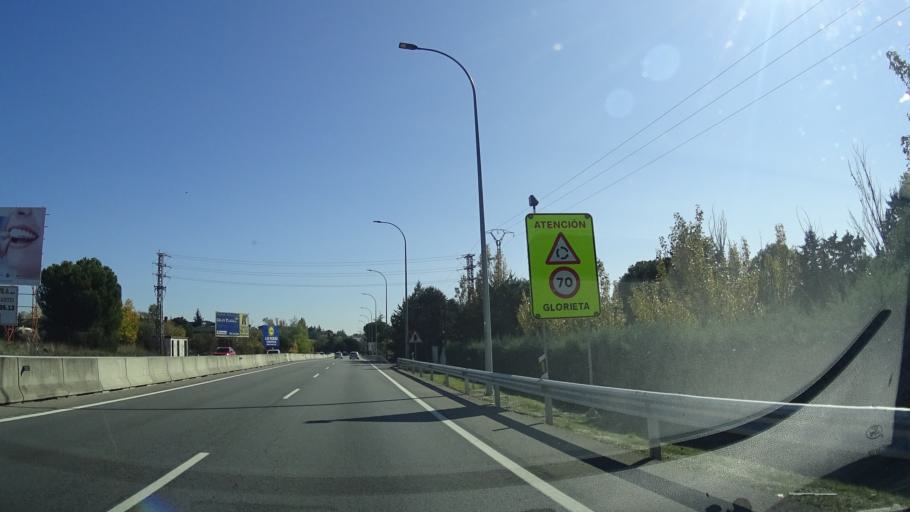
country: ES
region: Madrid
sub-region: Provincia de Madrid
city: Las Rozas de Madrid
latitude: 40.5055
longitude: -3.9101
